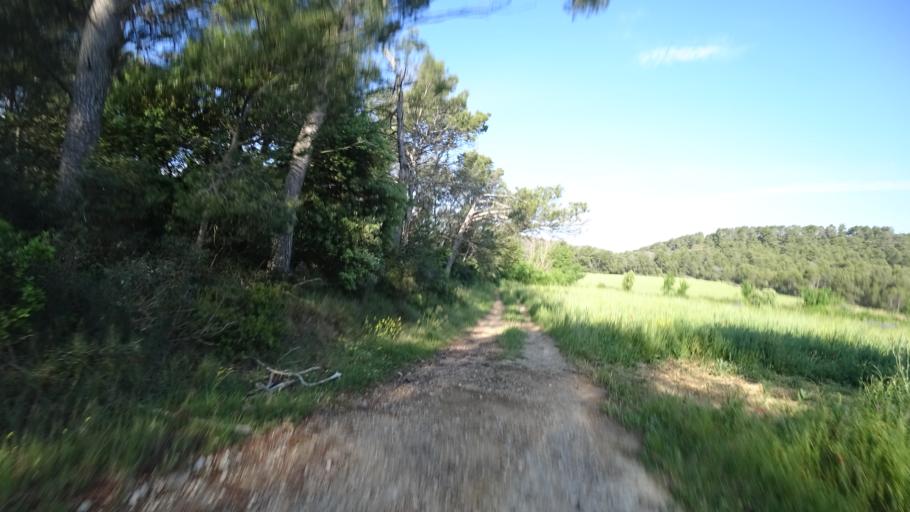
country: FR
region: Languedoc-Roussillon
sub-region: Departement de l'Aude
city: Lezignan-Corbieres
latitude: 43.2363
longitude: 2.7528
